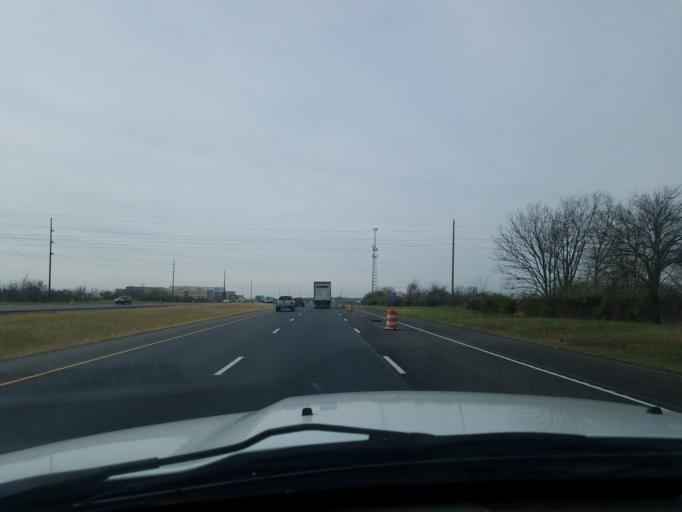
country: US
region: Indiana
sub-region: Hancock County
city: McCordsville
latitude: 39.9913
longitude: -85.9086
